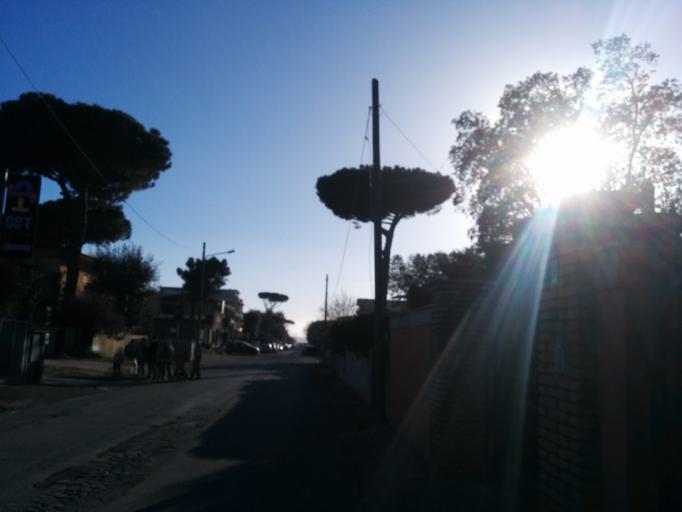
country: IT
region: Latium
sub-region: Citta metropolitana di Roma Capitale
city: Lavinio
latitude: 41.4981
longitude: 12.5911
